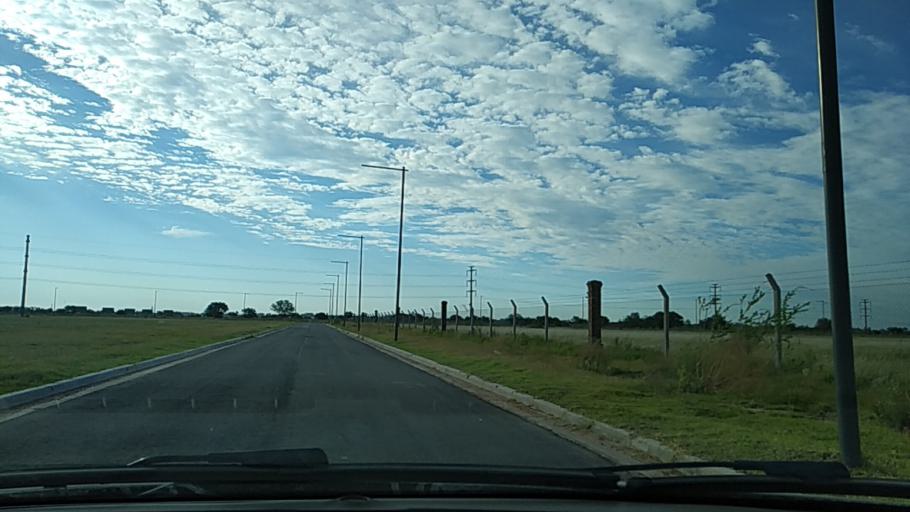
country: AR
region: Santa Fe
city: Funes
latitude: -32.9468
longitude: -60.7764
